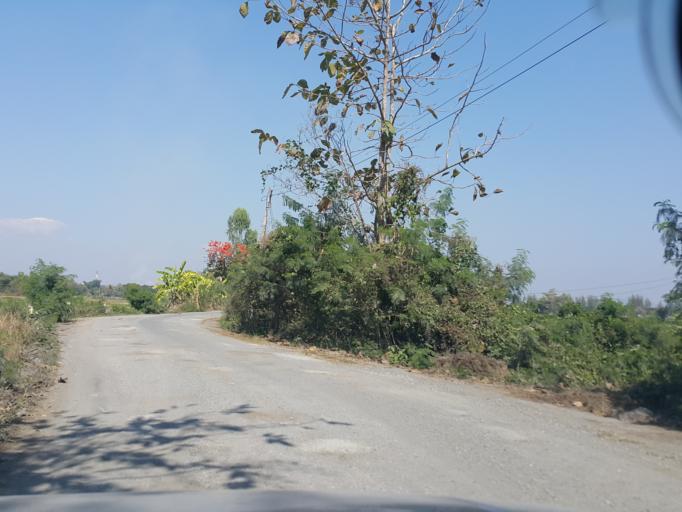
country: TH
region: Chiang Mai
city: San Kamphaeng
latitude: 18.7966
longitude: 99.1235
